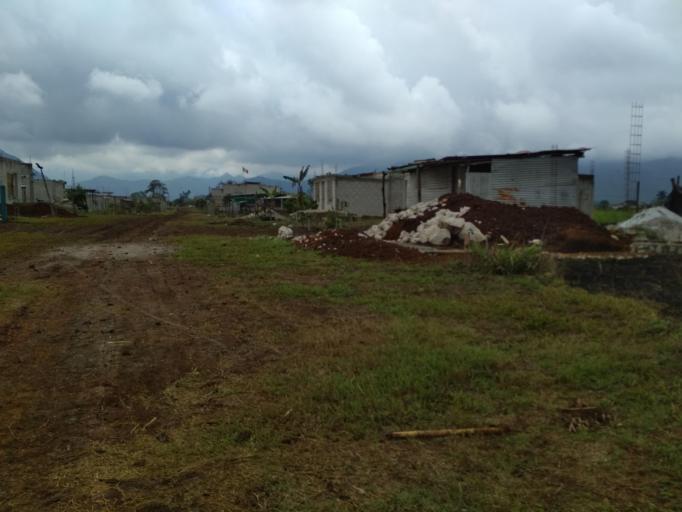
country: MX
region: Veracruz
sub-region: Cordoba
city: San Jose de Tapia
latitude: 18.8487
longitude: -96.9623
